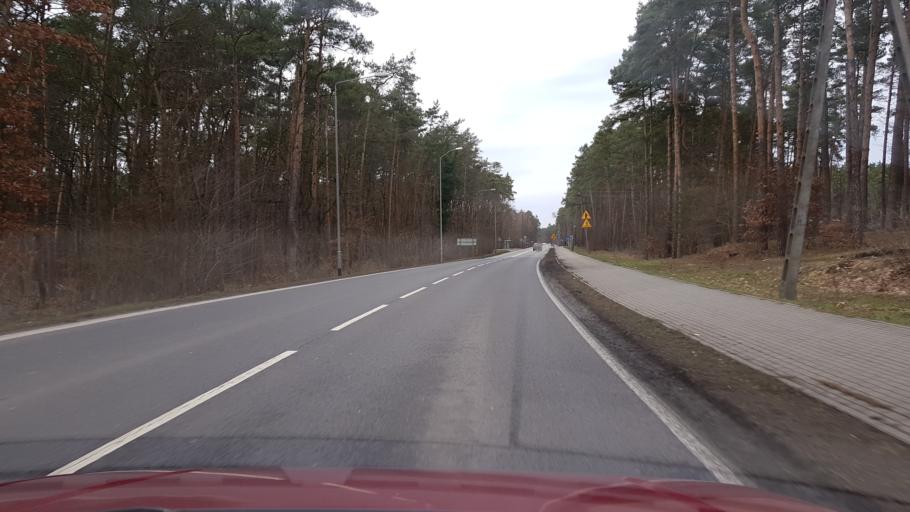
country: PL
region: West Pomeranian Voivodeship
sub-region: Powiat policki
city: Dobra
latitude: 53.5015
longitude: 14.4783
